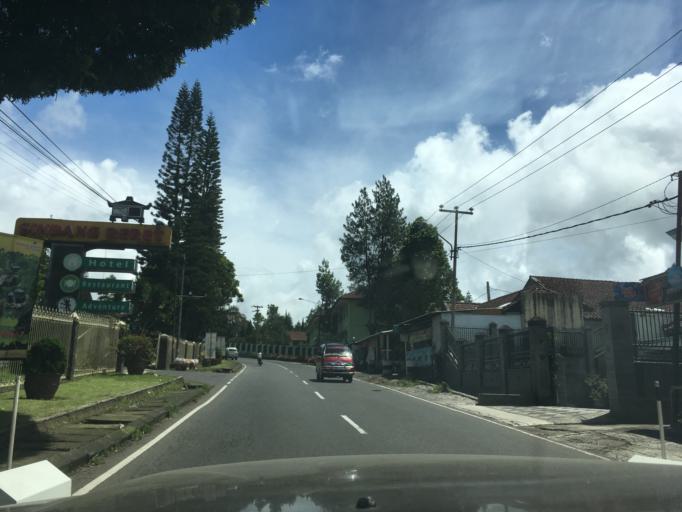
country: ID
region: West Java
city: Lembang
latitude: -6.7943
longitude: 107.6546
